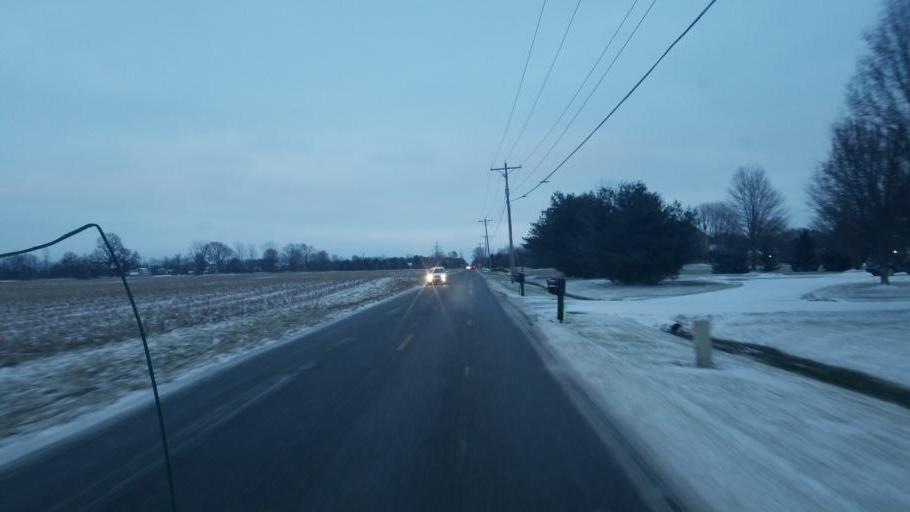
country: US
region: Ohio
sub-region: Delaware County
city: Sunbury
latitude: 40.1675
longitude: -82.8476
